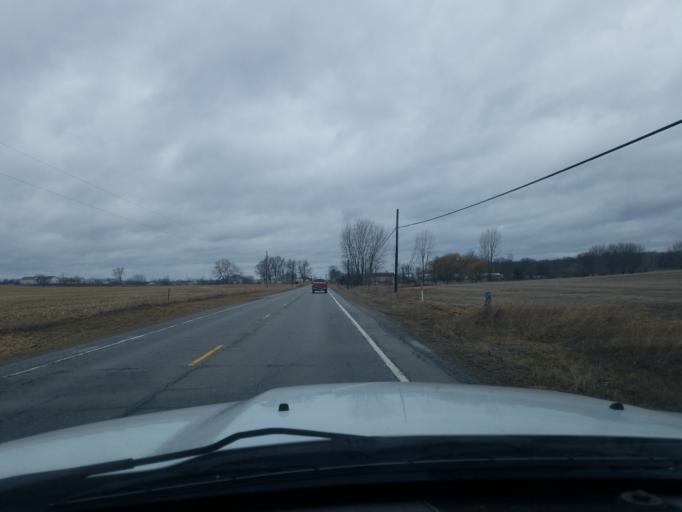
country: US
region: Indiana
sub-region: Noble County
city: Rome City
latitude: 41.4525
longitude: -85.3298
